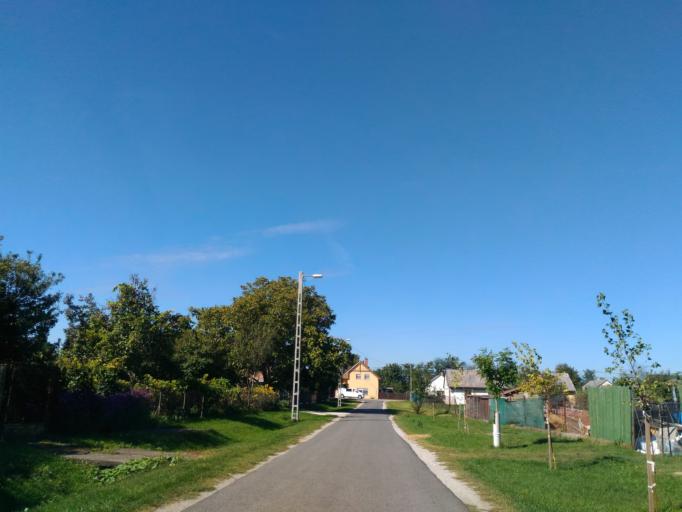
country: HU
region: Fejer
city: Ivancsa
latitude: 47.1816
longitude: 18.8218
